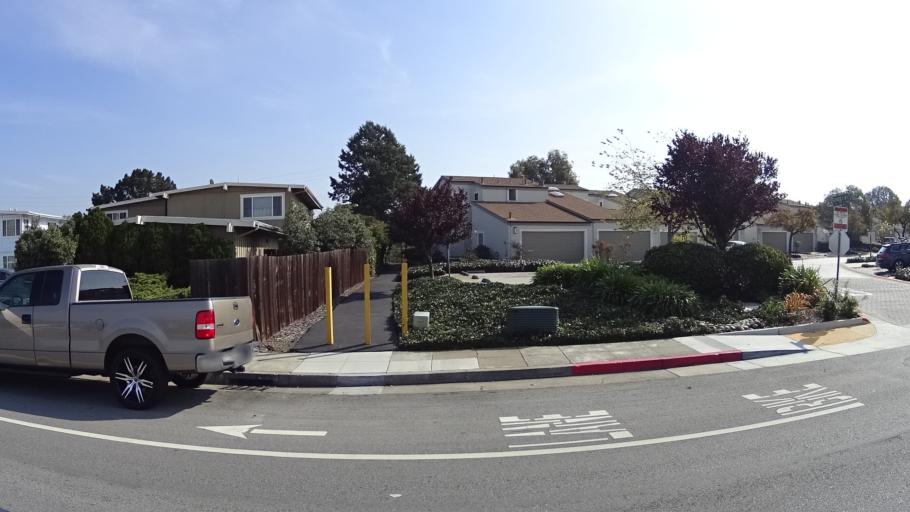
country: US
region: California
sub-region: San Mateo County
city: Belmont
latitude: 37.5399
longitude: -122.2790
